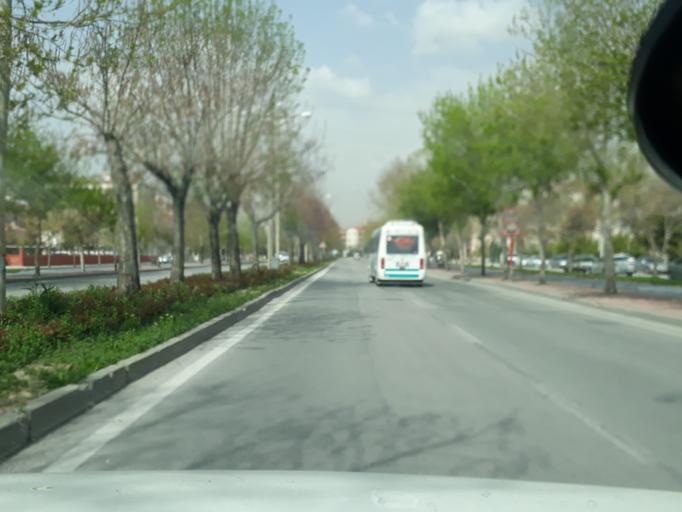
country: TR
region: Konya
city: Selcuklu
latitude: 37.9372
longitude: 32.4965
